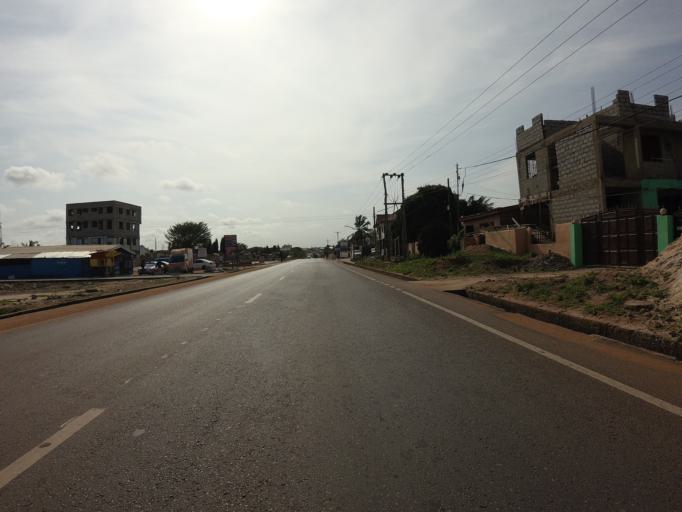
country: GH
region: Greater Accra
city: Nungua
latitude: 5.6450
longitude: -0.0964
